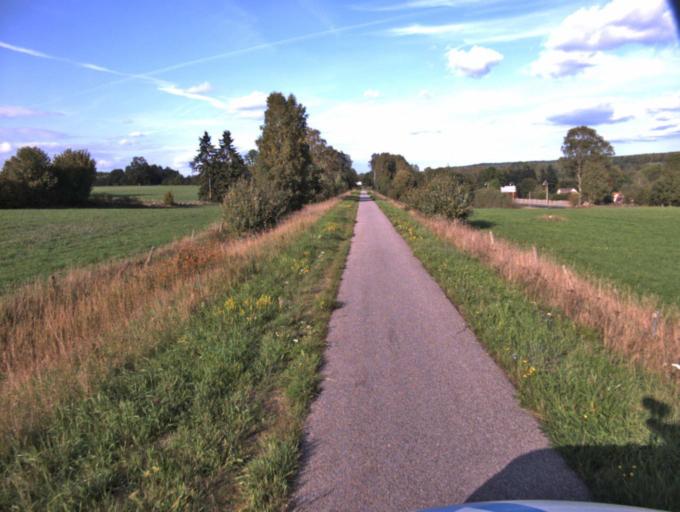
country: SE
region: Vaestra Goetaland
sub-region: Ulricehamns Kommun
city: Ulricehamn
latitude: 57.9165
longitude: 13.4837
